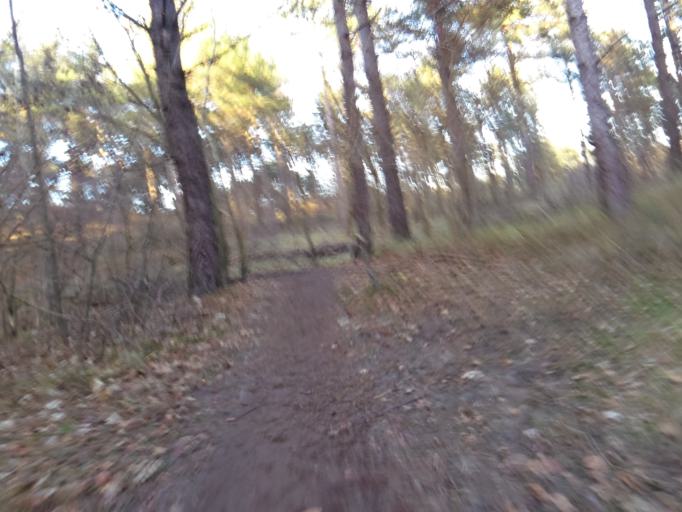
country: NL
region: South Holland
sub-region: Gemeente Noordwijk
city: Noordwijk-Binnen
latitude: 52.2647
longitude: 4.4585
